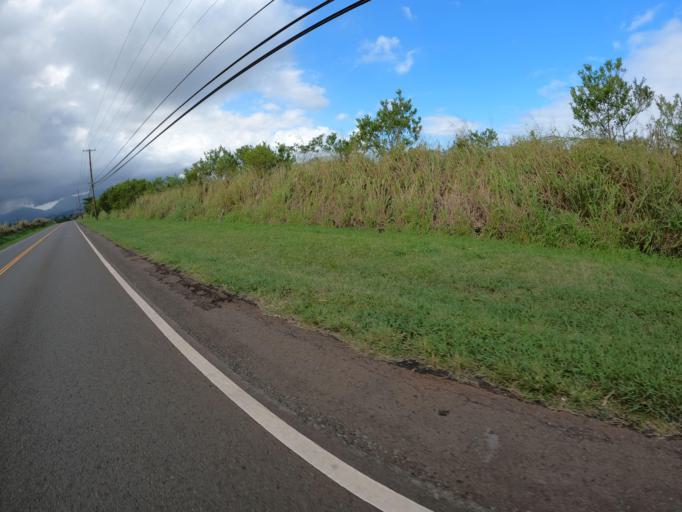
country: US
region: Hawaii
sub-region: Honolulu County
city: Whitmore Village
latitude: 21.5147
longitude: -158.0090
